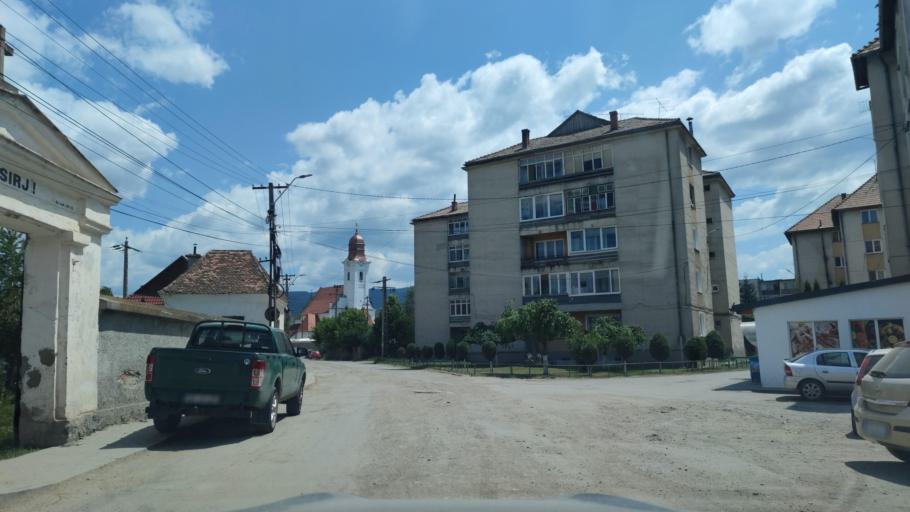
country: RO
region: Harghita
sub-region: Municipiul Gheorgheni
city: Gheorgheni
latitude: 46.7254
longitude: 25.6035
